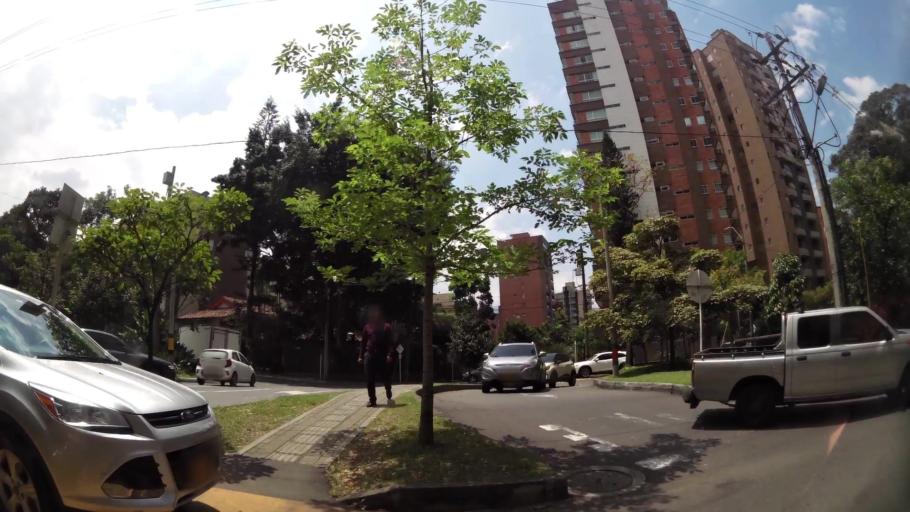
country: CO
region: Antioquia
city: Envigado
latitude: 6.1848
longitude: -75.5799
